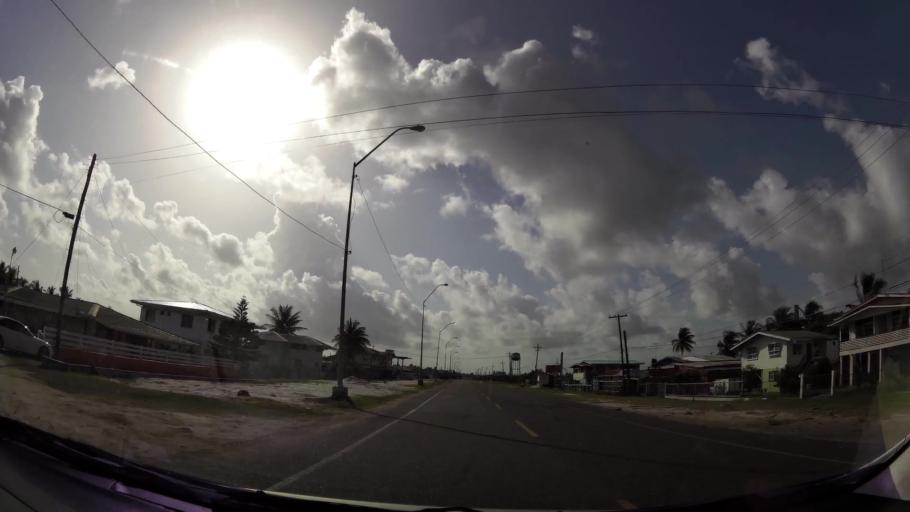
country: GY
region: Demerara-Mahaica
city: Georgetown
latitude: 6.8143
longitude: -58.0686
